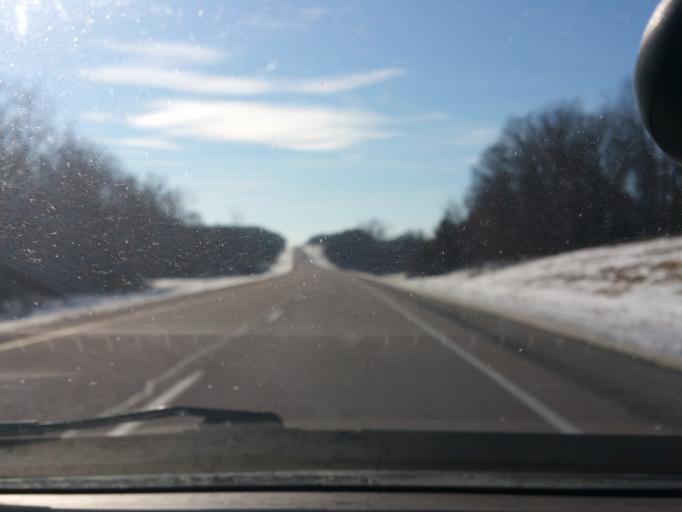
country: US
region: Iowa
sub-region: Decatur County
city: Leon
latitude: 40.7158
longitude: -93.8452
